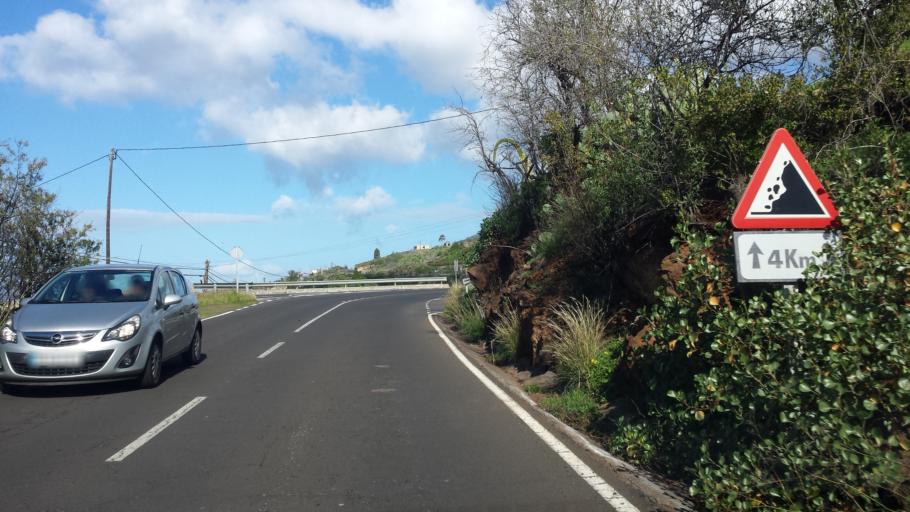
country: ES
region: Canary Islands
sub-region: Provincia de Santa Cruz de Tenerife
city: Tijarafe
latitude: 28.6793
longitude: -17.9447
